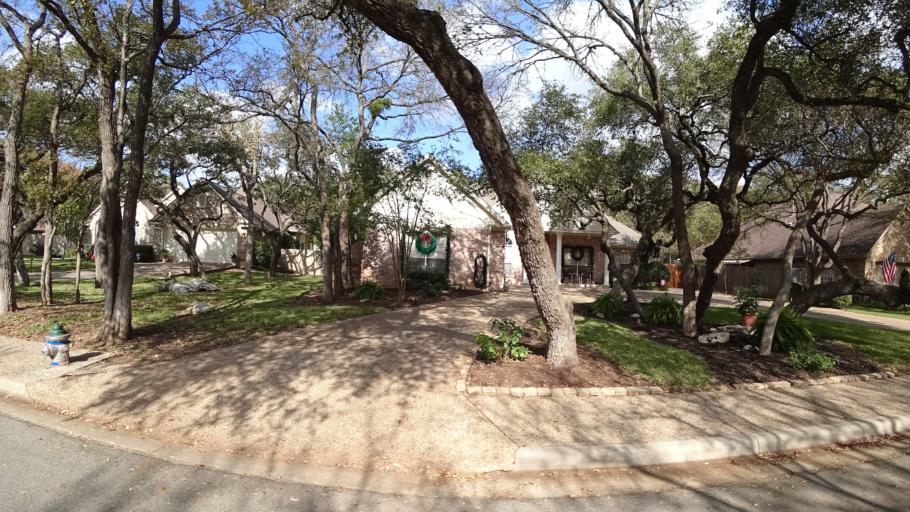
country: US
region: Texas
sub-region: Travis County
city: Shady Hollow
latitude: 30.1712
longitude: -97.8595
